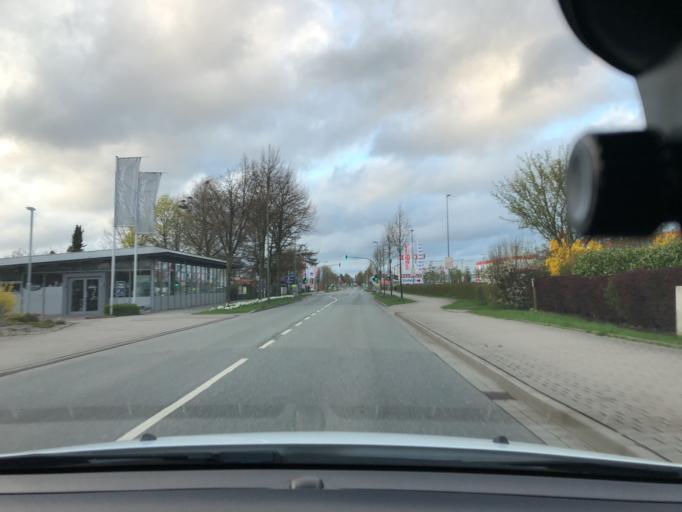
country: DE
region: Schleswig-Holstein
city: Flensburg
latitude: 54.7626
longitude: 9.4352
